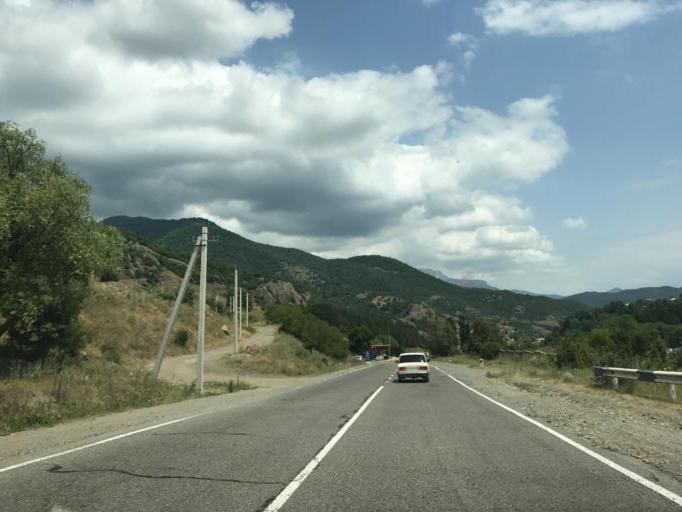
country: AM
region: Tavush
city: Dilijan
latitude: 40.7514
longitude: 44.8735
